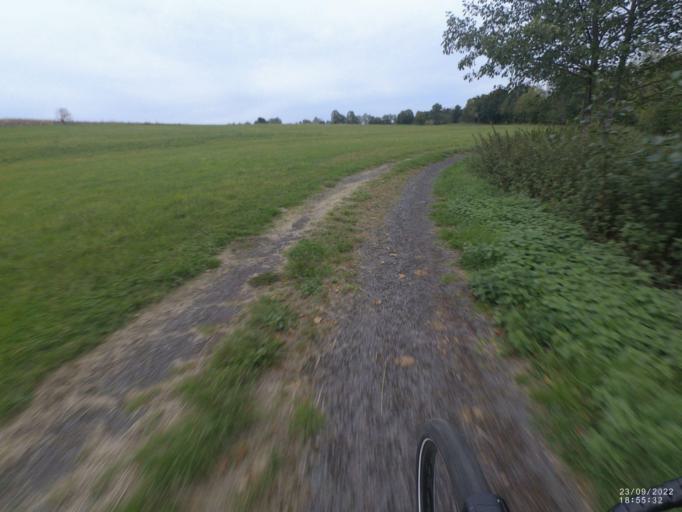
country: DE
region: Rheinland-Pfalz
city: Dockweiler
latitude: 50.2431
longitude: 6.7902
